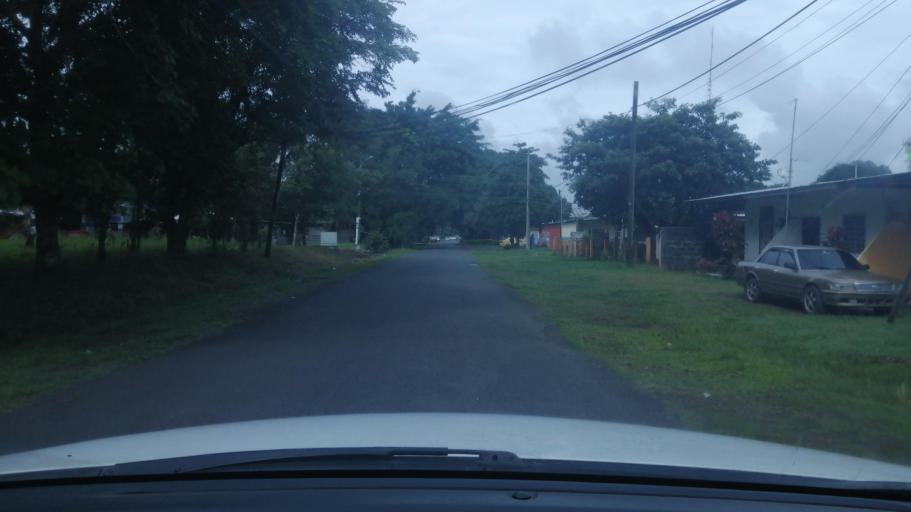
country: PA
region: Chiriqui
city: David
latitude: 8.4375
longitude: -82.4289
